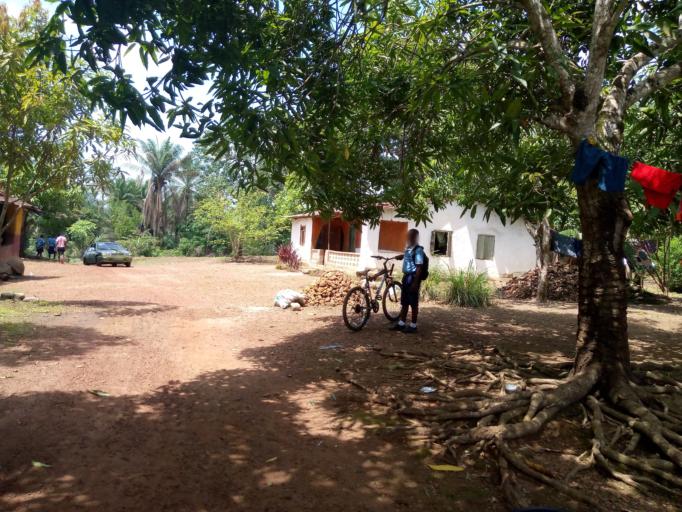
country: SL
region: Western Area
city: Waterloo
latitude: 8.3543
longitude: -12.9237
